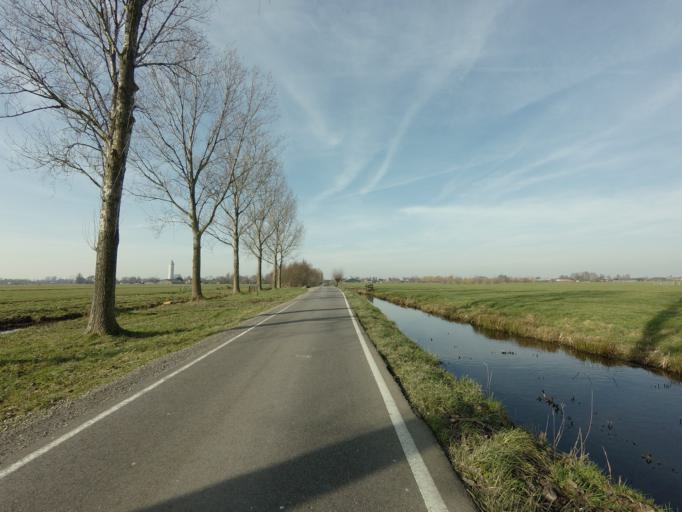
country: NL
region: South Holland
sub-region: Gemeente Nieuwkoop
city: Nieuwkoop
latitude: 52.1190
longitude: 4.7995
